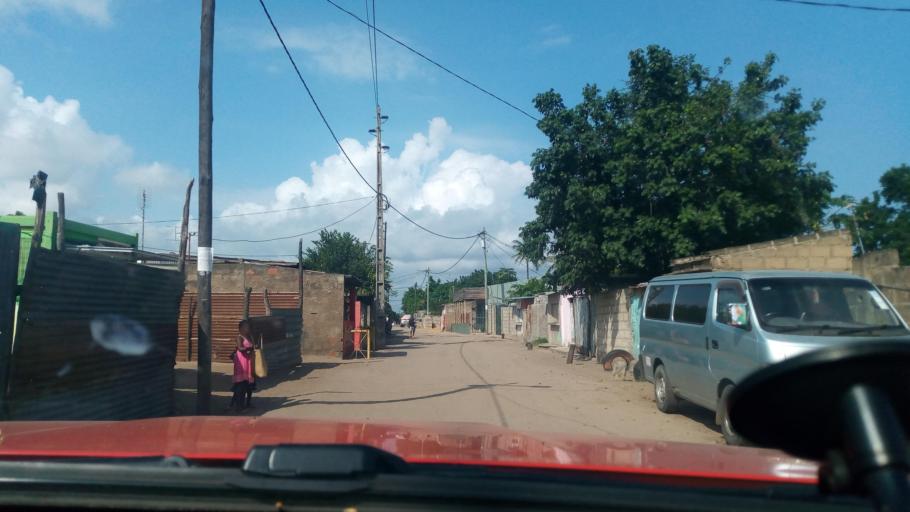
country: MZ
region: Maputo City
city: Maputo
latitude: -25.9168
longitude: 32.5627
